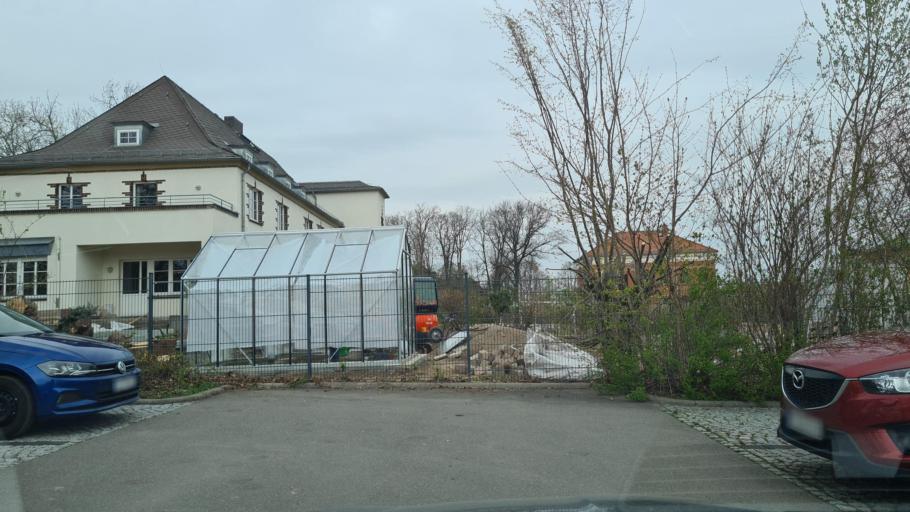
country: DE
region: Saxony
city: Zwickau
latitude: 50.7338
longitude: 12.4846
